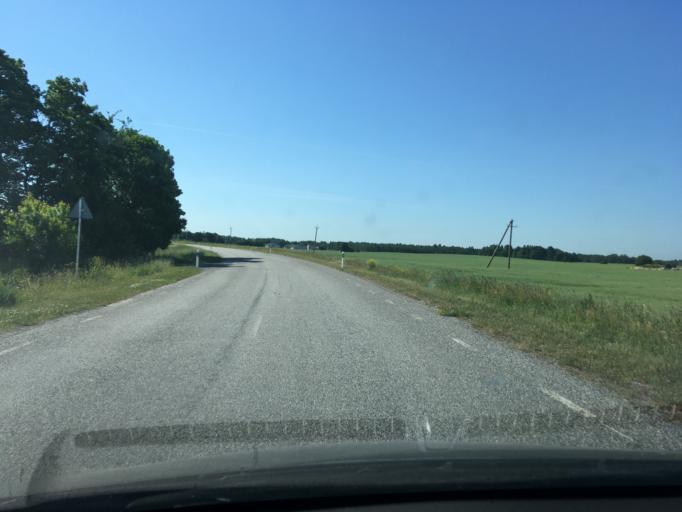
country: EE
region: Harju
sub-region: Raasiku vald
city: Raasiku
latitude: 59.3952
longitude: 25.1866
